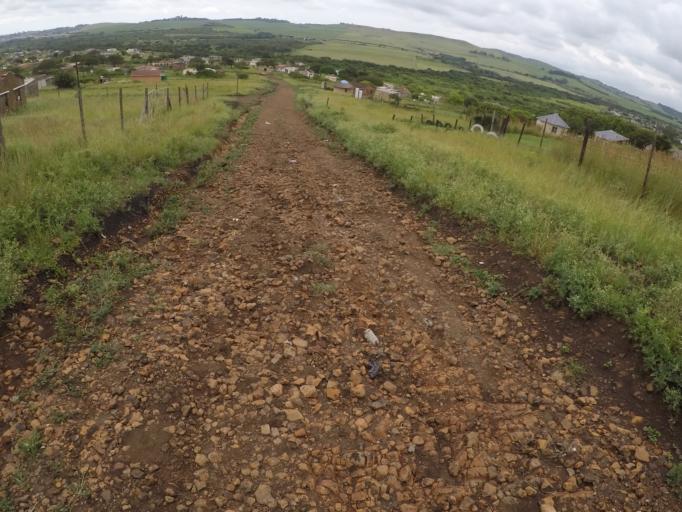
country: ZA
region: KwaZulu-Natal
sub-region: uThungulu District Municipality
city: Empangeni
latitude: -28.7099
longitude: 31.8521
